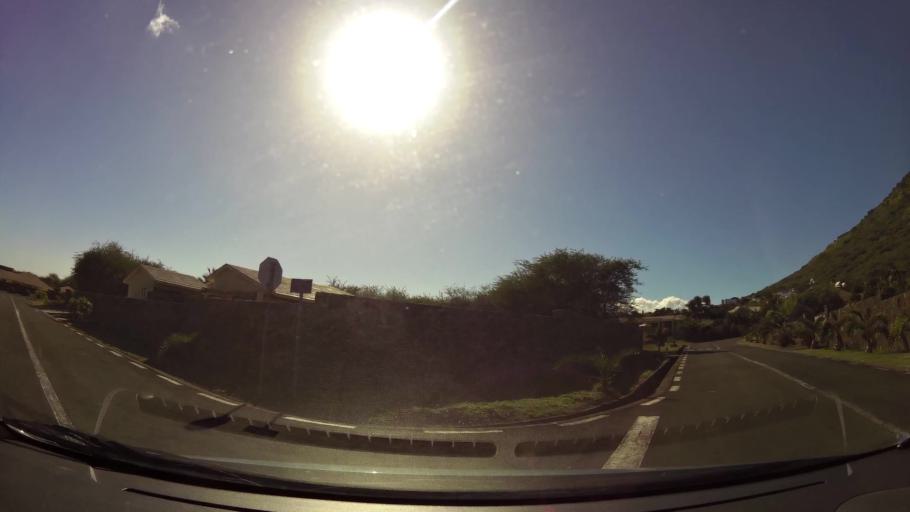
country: MU
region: Black River
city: Tamarin
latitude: -20.3408
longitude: 57.3669
